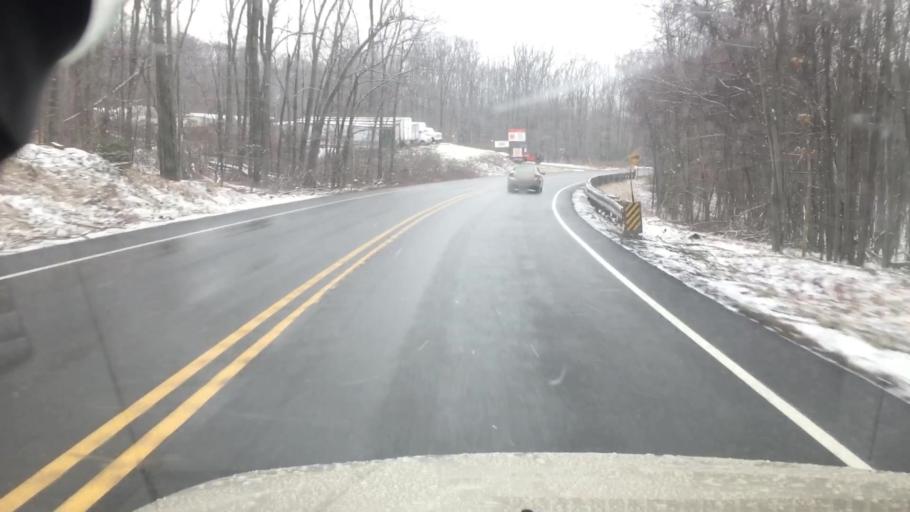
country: US
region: Pennsylvania
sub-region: Luzerne County
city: Conyngham
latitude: 41.0310
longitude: -76.0819
